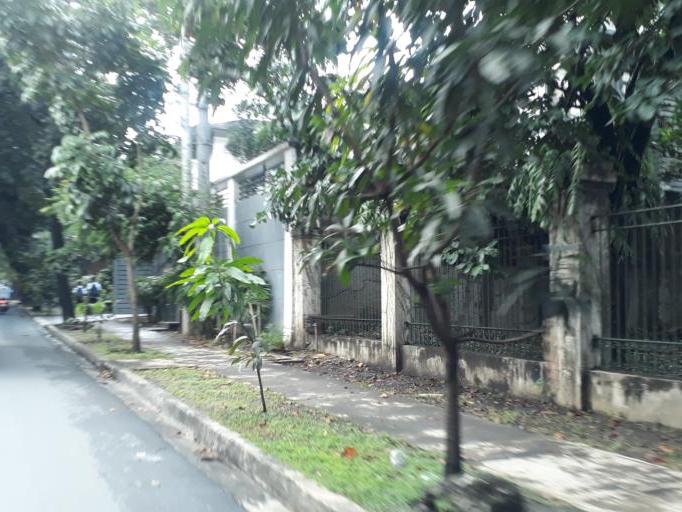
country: PH
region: Calabarzon
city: Del Monte
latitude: 14.6217
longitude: 121.0269
